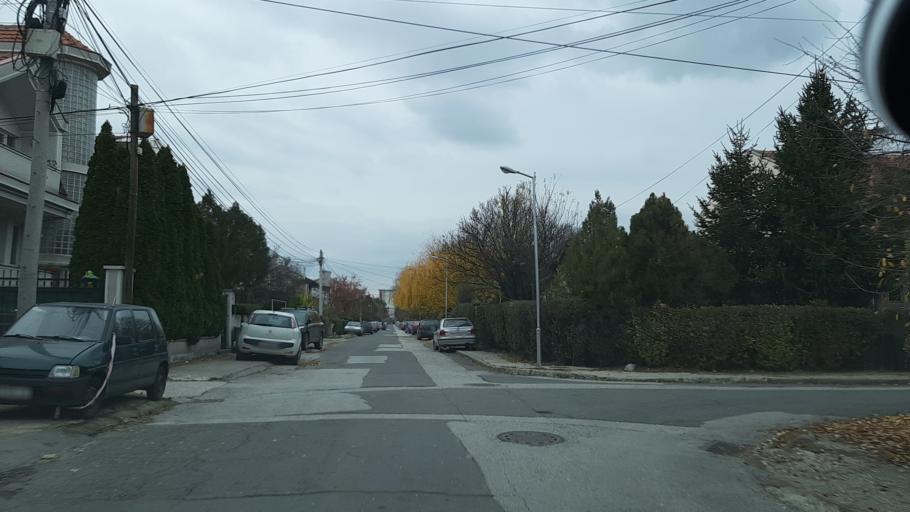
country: MK
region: Kisela Voda
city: Usje
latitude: 41.9735
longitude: 21.4689
